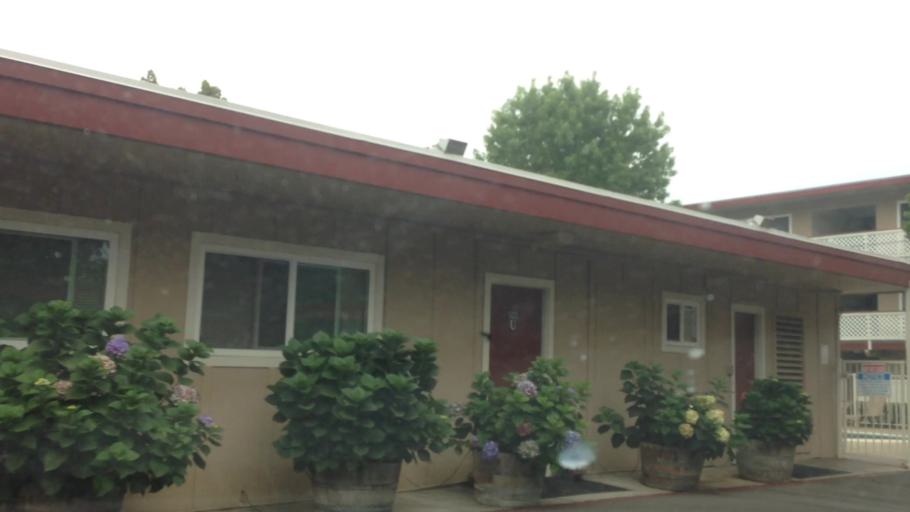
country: US
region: California
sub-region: Santa Clara County
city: Mountain View
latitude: 37.3968
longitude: -122.0750
